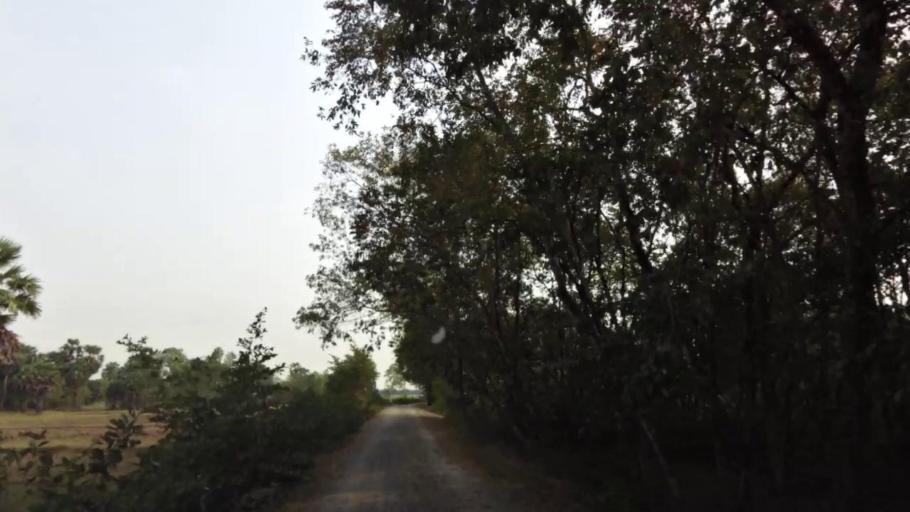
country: TH
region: Phra Nakhon Si Ayutthaya
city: Phra Nakhon Si Ayutthaya
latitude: 14.3424
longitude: 100.5676
